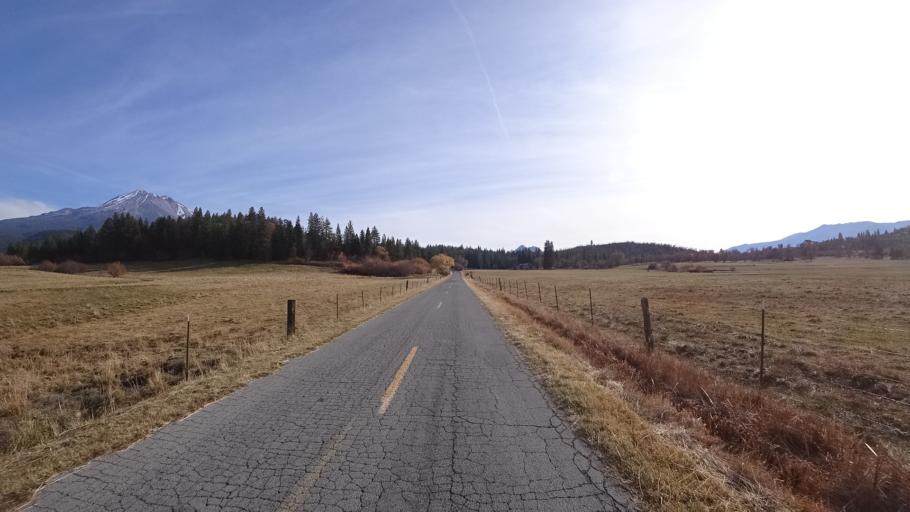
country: US
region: California
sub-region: Siskiyou County
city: Weed
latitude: 41.4521
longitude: -122.3825
